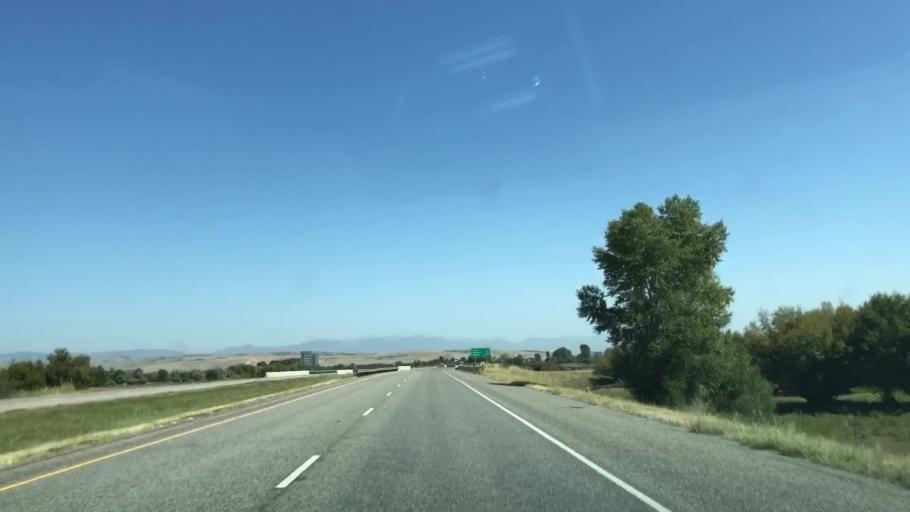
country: US
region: Montana
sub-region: Gallatin County
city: Three Forks
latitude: 45.8969
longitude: -111.5110
